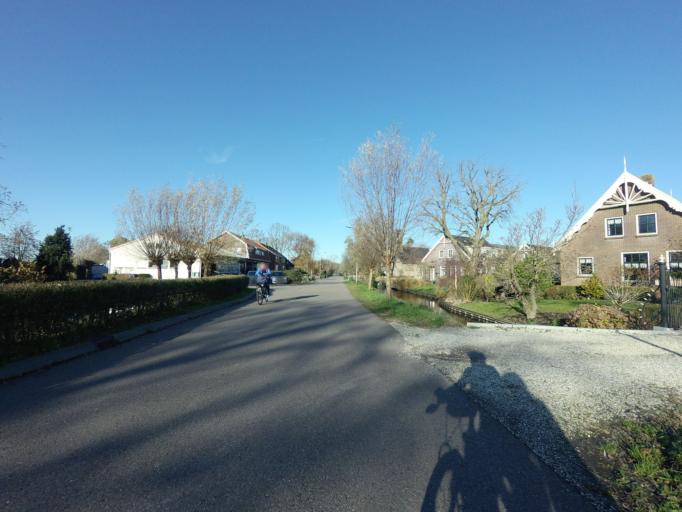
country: NL
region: South Holland
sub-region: Gemeente Nieuwkoop
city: Nieuwkoop
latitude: 52.1447
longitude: 4.7266
